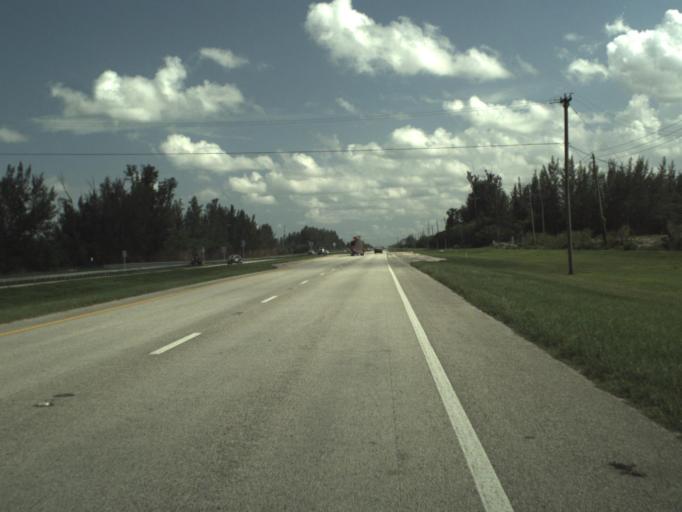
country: US
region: Florida
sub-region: Palm Beach County
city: Villages of Oriole
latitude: 26.4859
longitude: -80.2050
